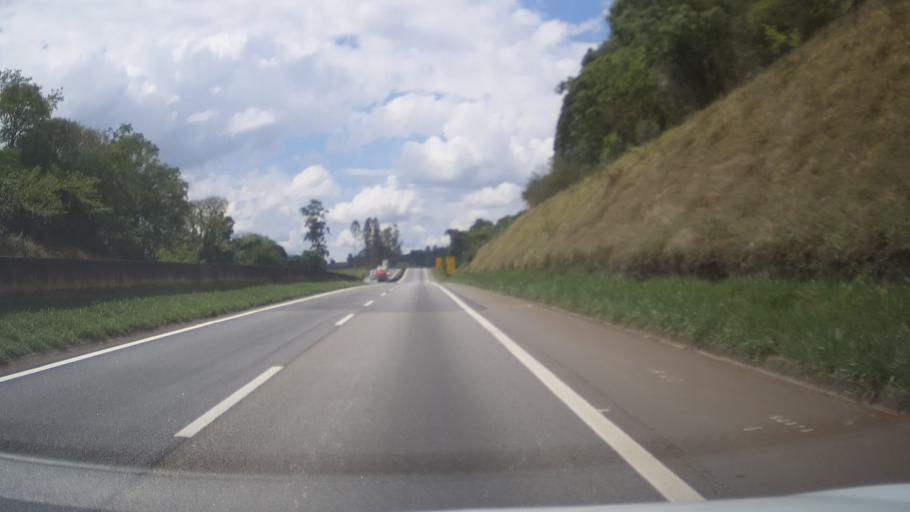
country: BR
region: Minas Gerais
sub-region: Nepomuceno
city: Nepomuceno
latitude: -21.2941
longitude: -45.1489
